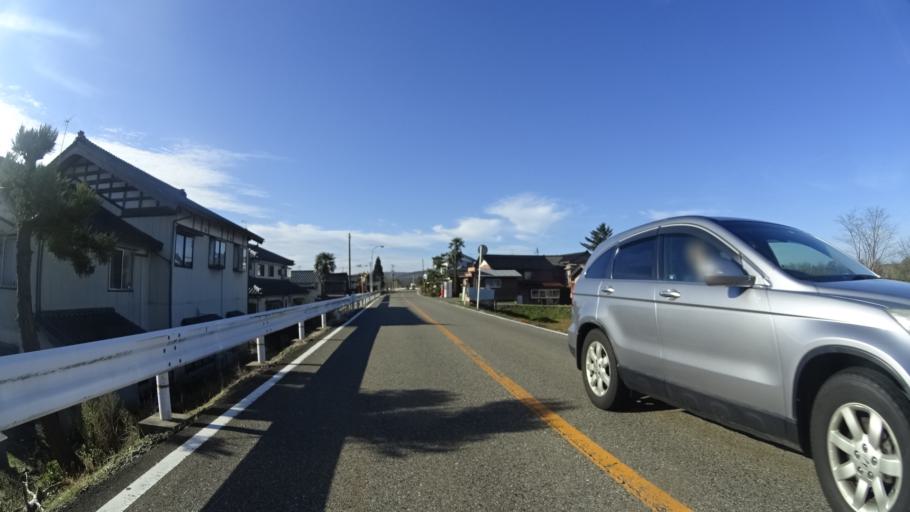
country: JP
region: Niigata
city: Yoshida-kasugacho
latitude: 37.5913
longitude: 138.8392
